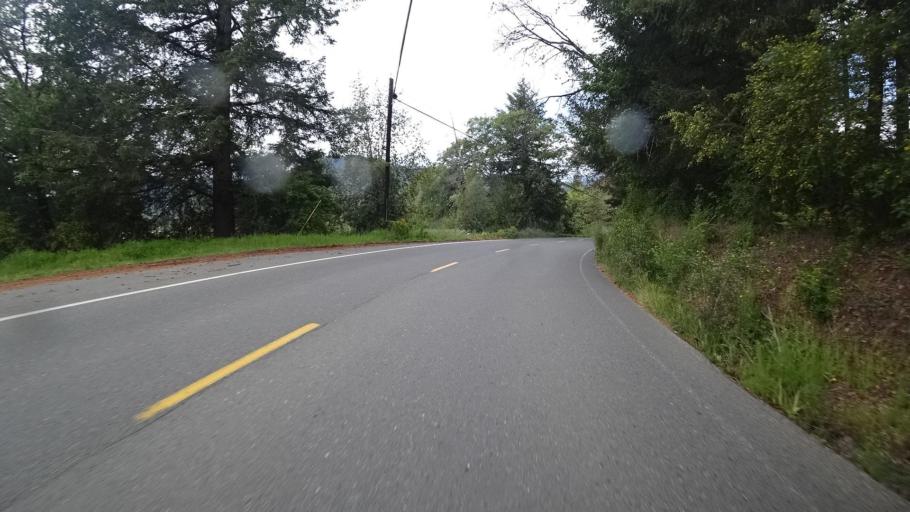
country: US
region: California
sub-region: Humboldt County
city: Redway
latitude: 40.1052
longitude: -123.7885
